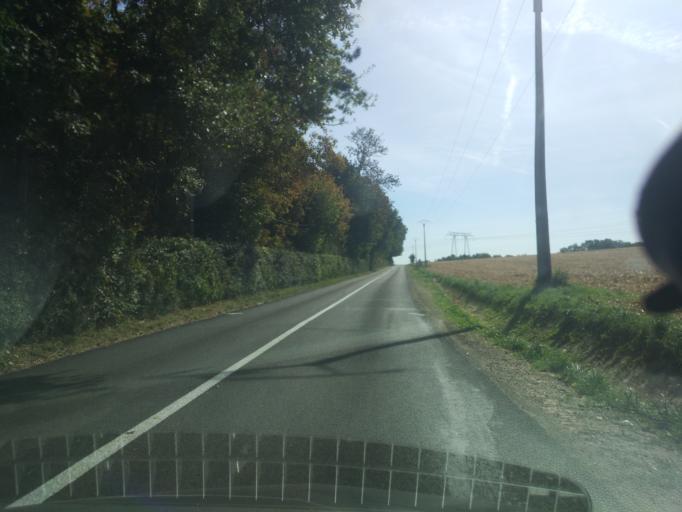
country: FR
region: Ile-de-France
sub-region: Departement de l'Essonne
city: Forges-les-Bains
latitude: 48.6398
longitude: 2.1006
